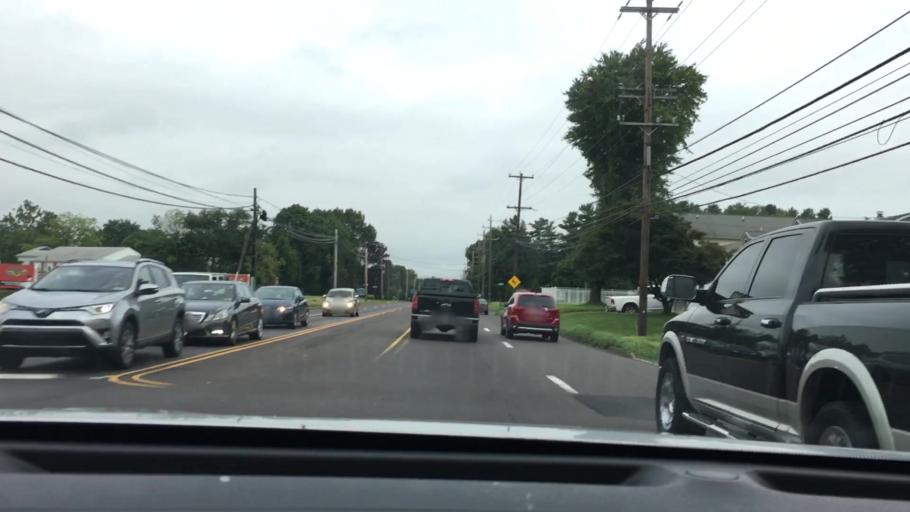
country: US
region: Pennsylvania
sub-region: Montgomery County
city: Hatboro
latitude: 40.1924
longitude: -75.1070
